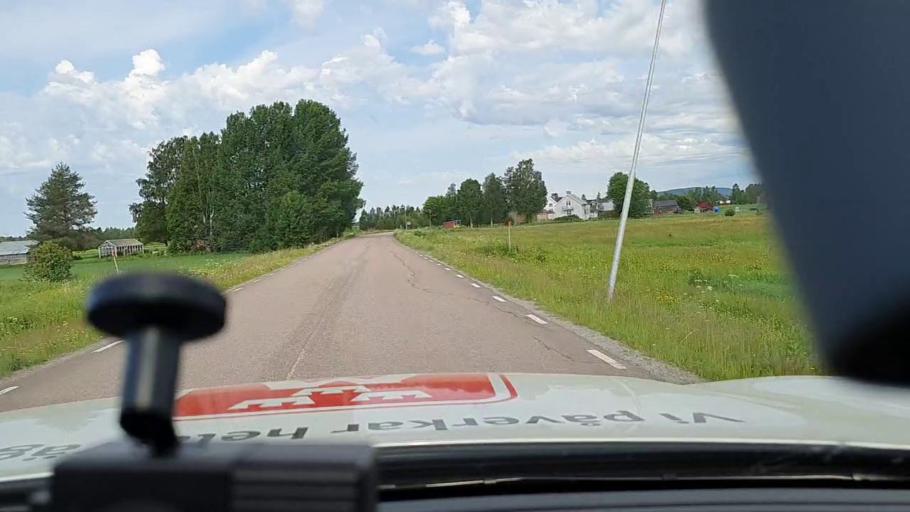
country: SE
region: Norrbotten
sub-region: Bodens Kommun
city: Saevast
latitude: 65.6846
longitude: 21.7916
